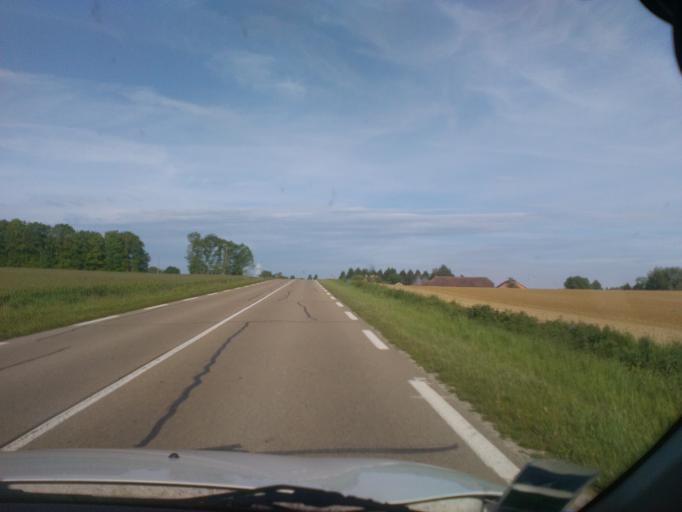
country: FR
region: Champagne-Ardenne
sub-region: Departement de l'Aube
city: Vendeuvre-sur-Barse
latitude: 48.2418
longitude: 4.3705
